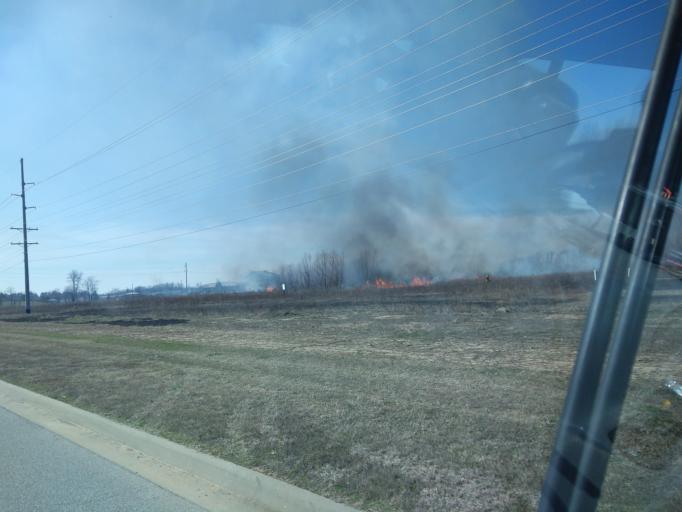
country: US
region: Arkansas
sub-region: Washington County
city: Farmington
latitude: 36.0671
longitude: -94.2310
